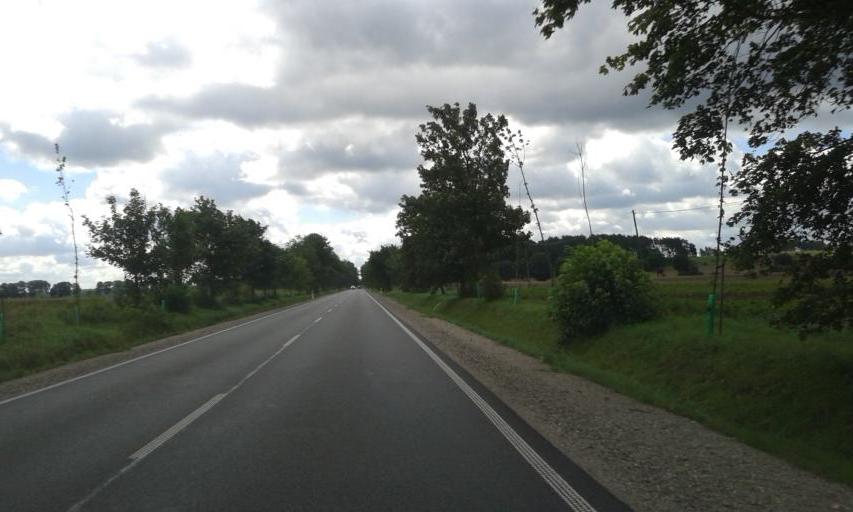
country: PL
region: West Pomeranian Voivodeship
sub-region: Powiat drawski
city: Czaplinek
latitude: 53.5108
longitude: 16.3206
